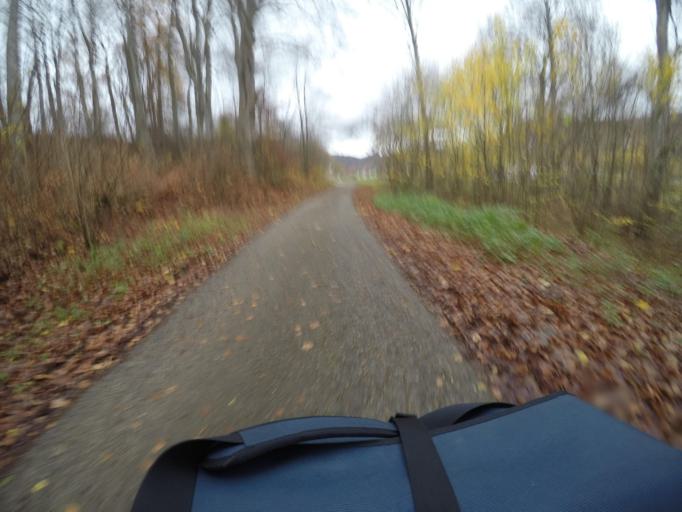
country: DE
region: Baden-Wuerttemberg
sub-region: Tuebingen Region
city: Pfullingen
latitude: 48.4000
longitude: 9.2726
